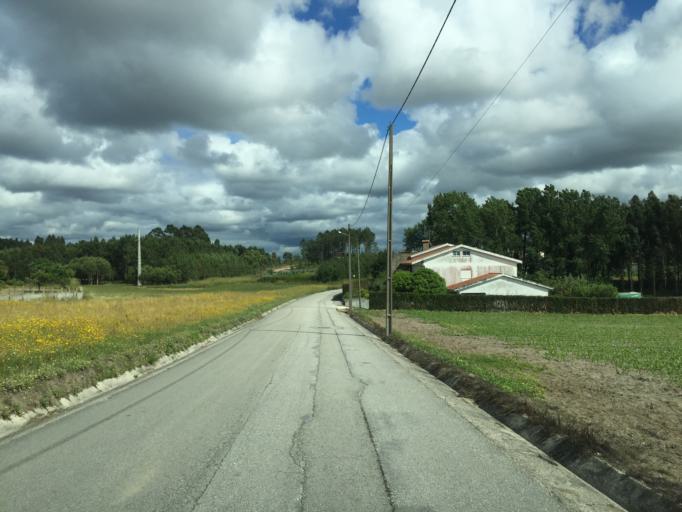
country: PT
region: Leiria
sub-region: Pombal
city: Lourical
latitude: 39.9812
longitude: -8.8053
